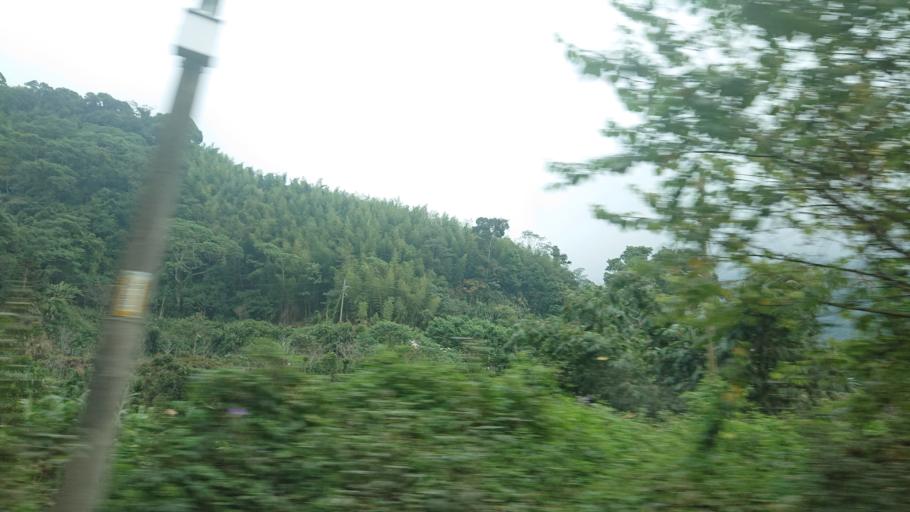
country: TW
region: Taiwan
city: Lugu
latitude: 23.6090
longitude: 120.7097
